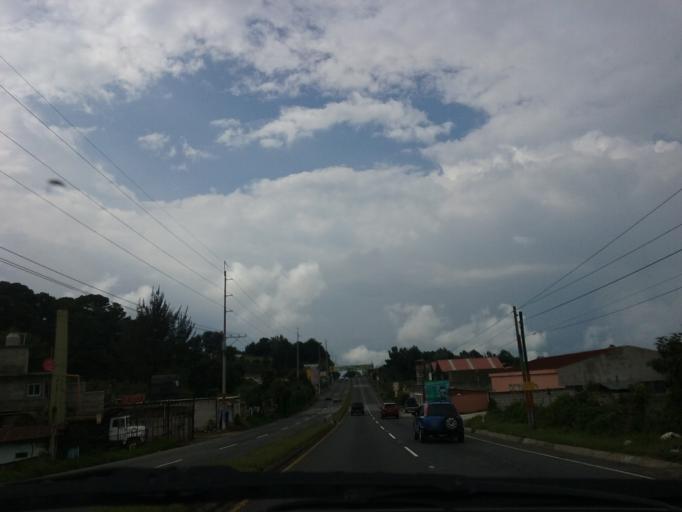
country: GT
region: Sacatepequez
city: Santiago Sacatepequez
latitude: 14.6287
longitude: -90.6866
